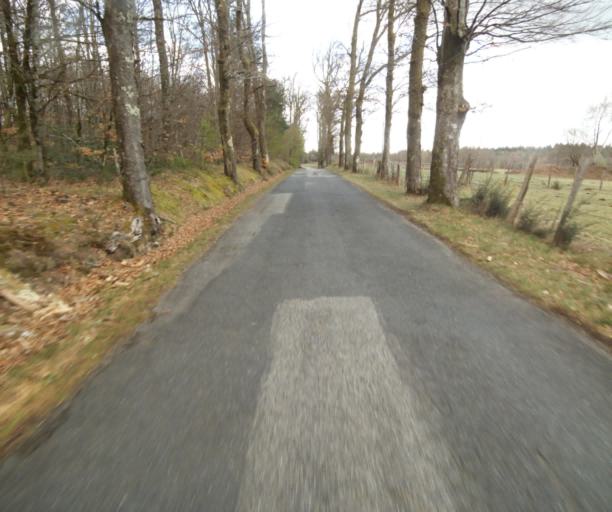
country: FR
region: Limousin
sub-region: Departement de la Correze
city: Correze
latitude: 45.2565
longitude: 1.9163
